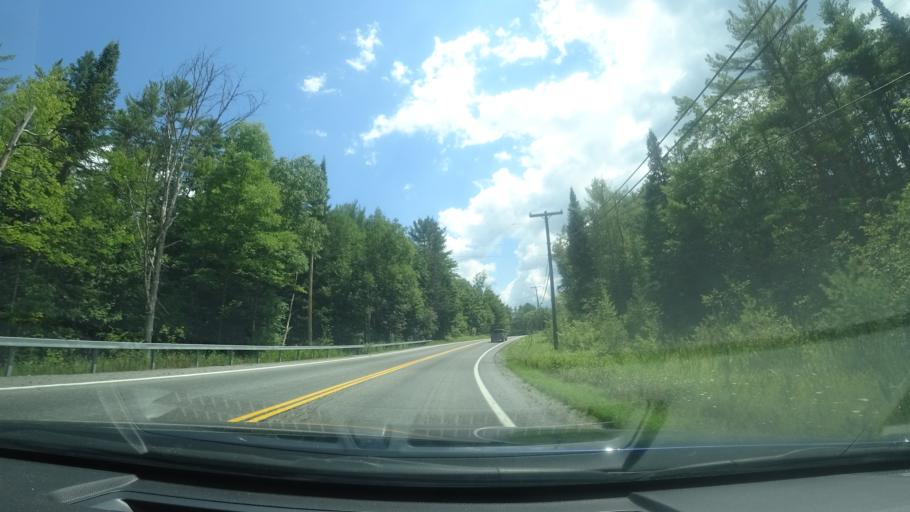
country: US
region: New York
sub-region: Warren County
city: Warrensburg
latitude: 43.6646
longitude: -73.8289
